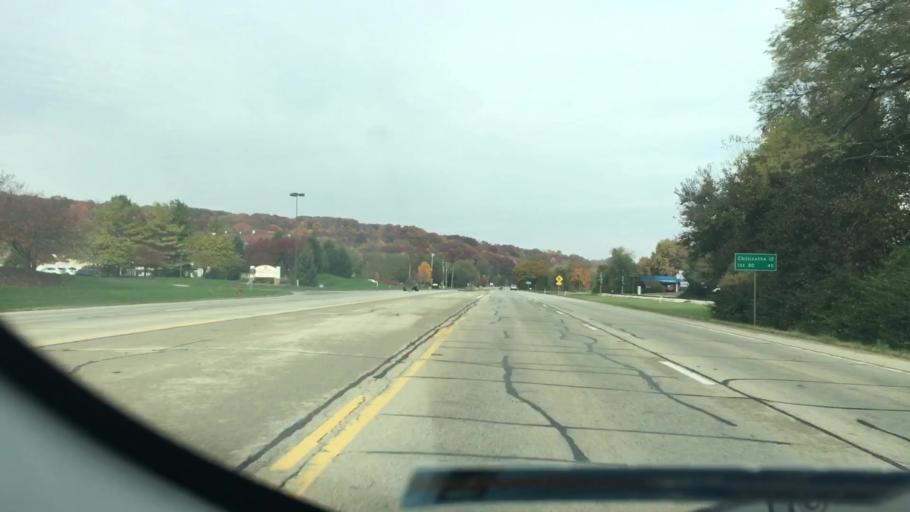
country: US
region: Illinois
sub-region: Peoria County
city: Peoria Heights
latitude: 40.7697
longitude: -89.5721
